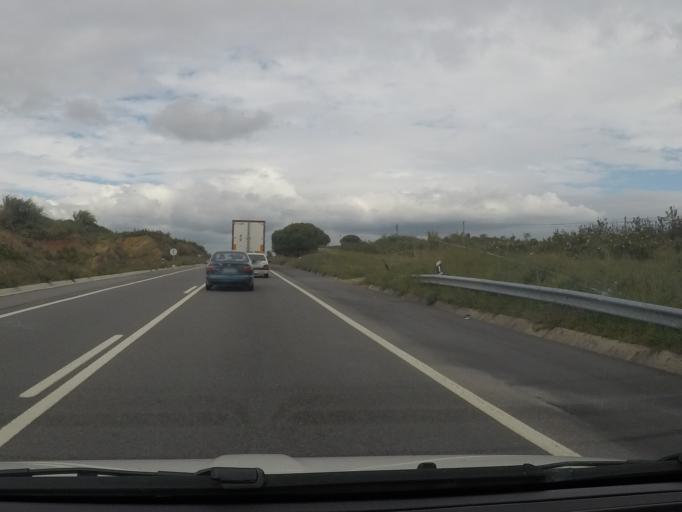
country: PT
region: Setubal
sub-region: Santiago do Cacem
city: Santiago do Cacem
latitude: 38.0689
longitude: -8.6824
